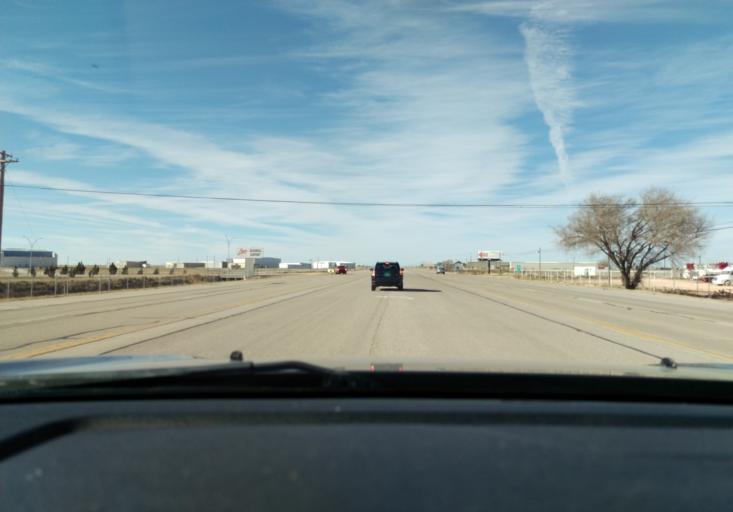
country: US
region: New Mexico
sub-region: Lea County
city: Hobbs
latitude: 32.6967
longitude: -103.2127
